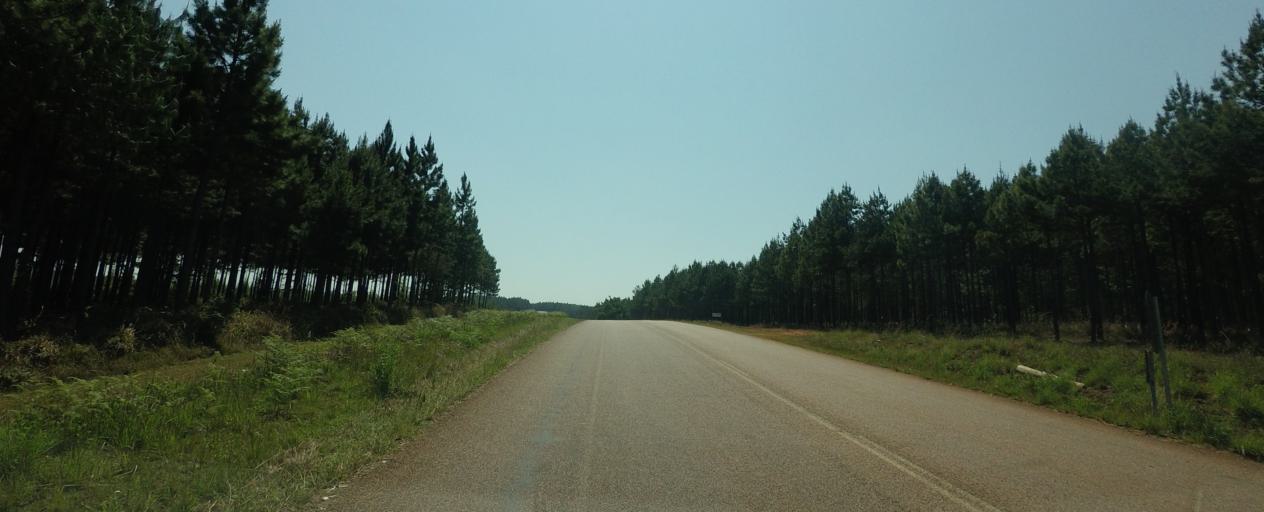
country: ZA
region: Mpumalanga
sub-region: Ehlanzeni District
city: Graksop
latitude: -25.0647
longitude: 30.8120
